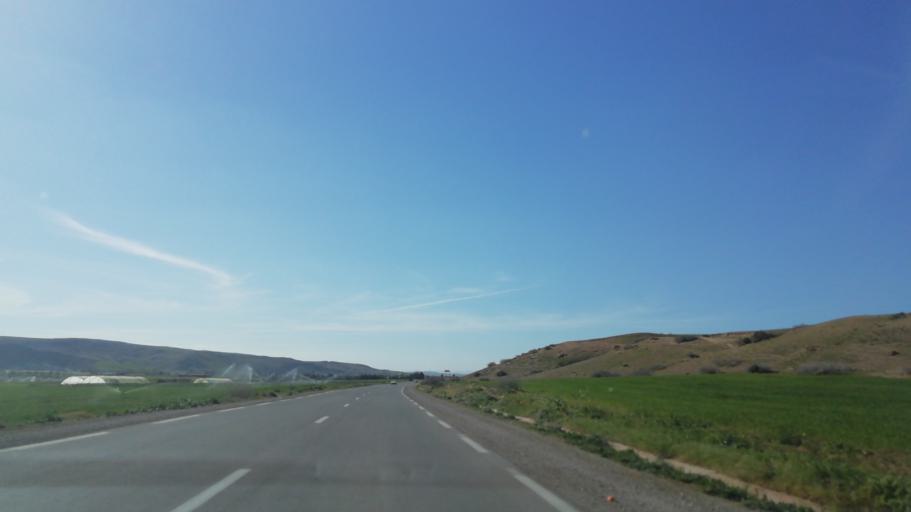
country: DZ
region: Mascara
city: Oued el Abtal
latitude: 35.4497
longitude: 0.7912
